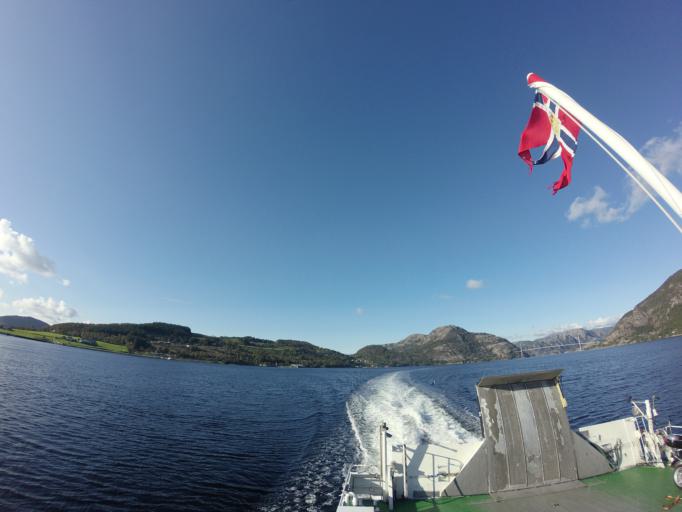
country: NO
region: Rogaland
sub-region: Forsand
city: Forsand
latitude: 58.9043
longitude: 6.0864
